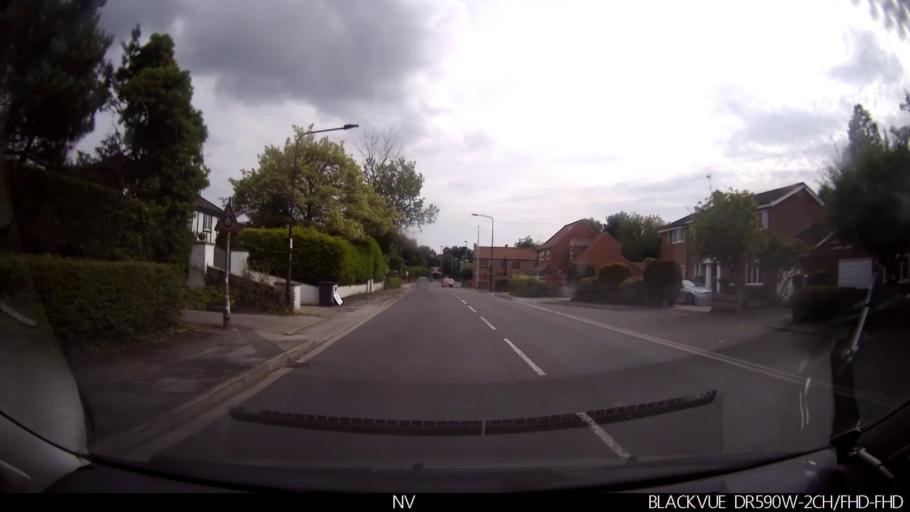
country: GB
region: England
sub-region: City of York
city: Huntington
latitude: 54.0062
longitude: -1.0552
